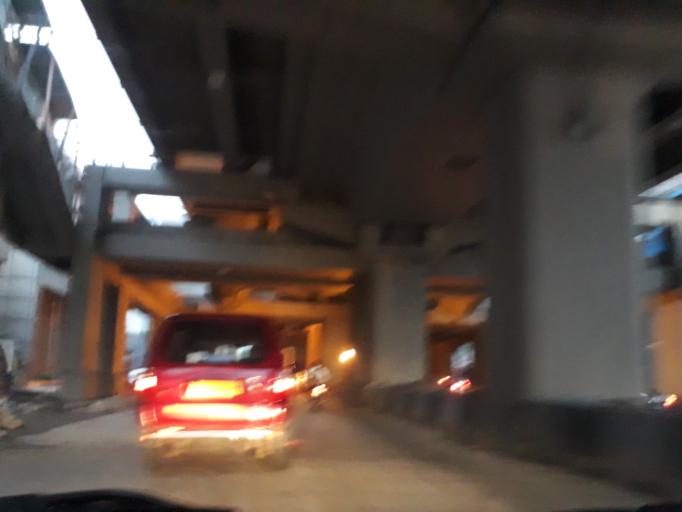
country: IN
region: Telangana
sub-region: Rangareddi
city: Kukatpalli
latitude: 17.4277
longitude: 78.4142
